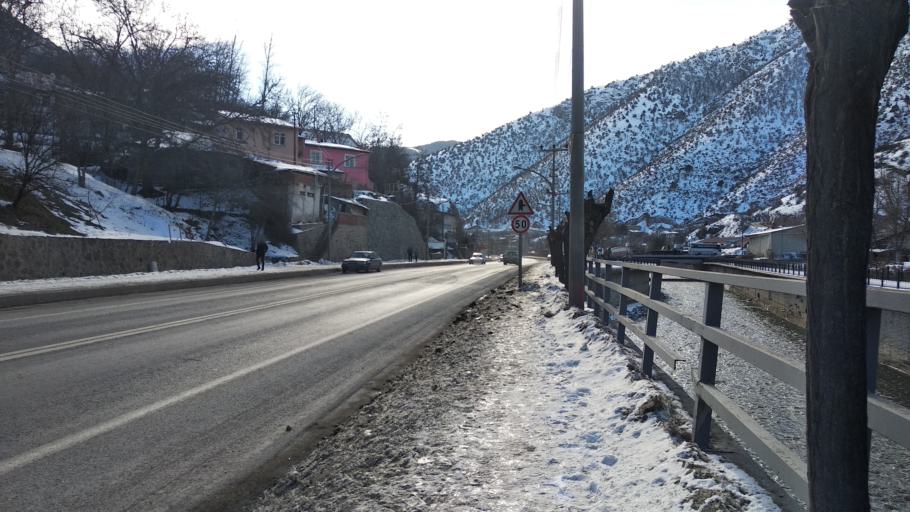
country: TR
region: Gumushane
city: Gumushkhane
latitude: 40.4421
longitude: 39.5036
